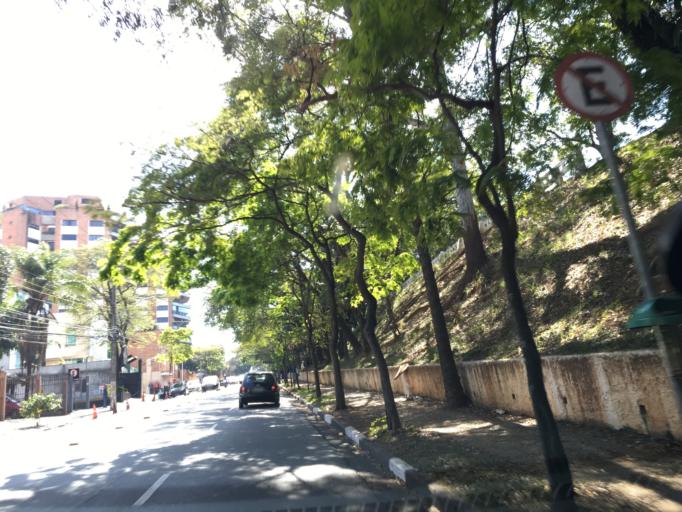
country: BR
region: Sao Paulo
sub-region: Sao Paulo
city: Sao Paulo
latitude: -23.5388
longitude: -46.7125
